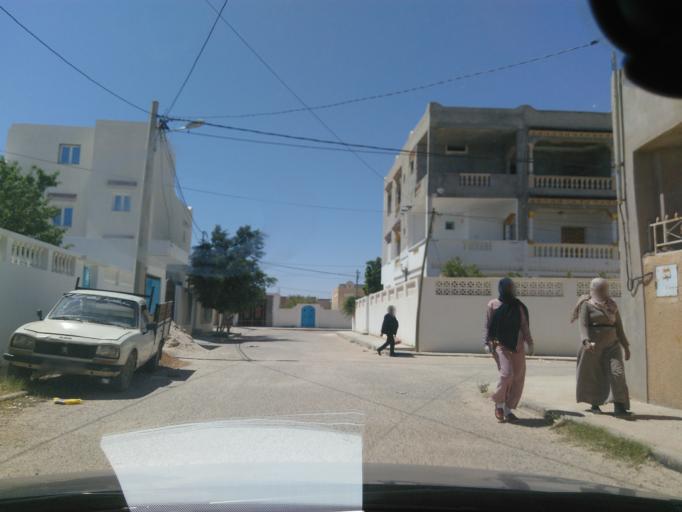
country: TN
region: Tataouine
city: Tataouine
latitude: 32.9475
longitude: 10.4640
